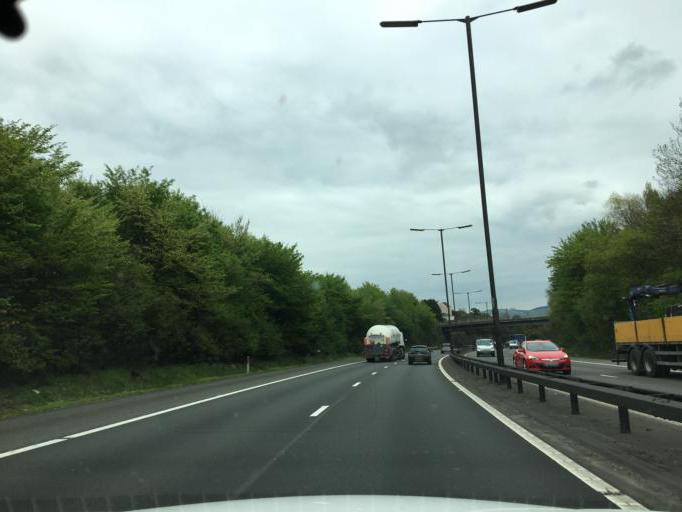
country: GB
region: Wales
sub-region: Neath Port Talbot
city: Briton Ferry
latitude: 51.6577
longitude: -3.8569
